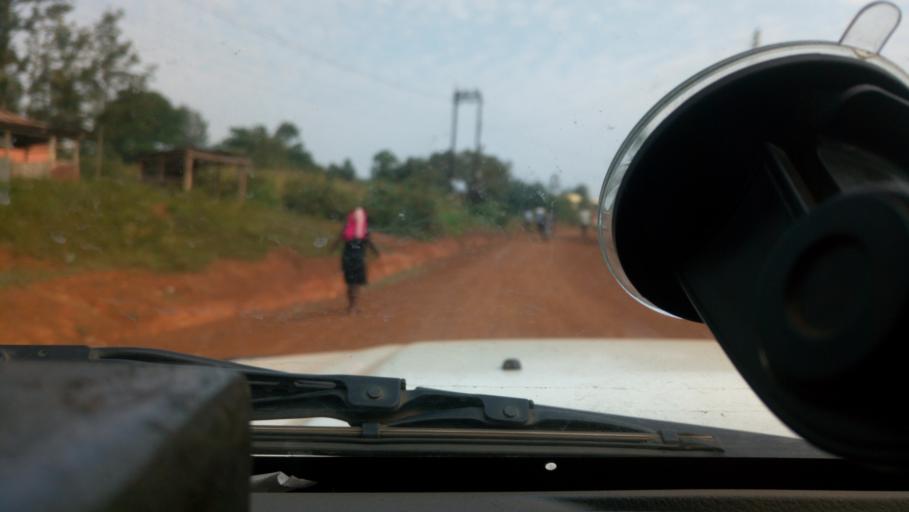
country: KE
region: Migori
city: Migori
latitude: -0.9849
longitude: 34.4991
